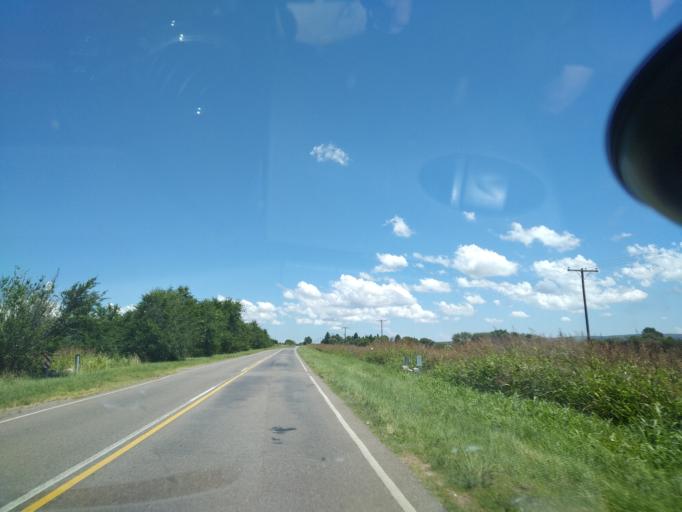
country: AR
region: Cordoba
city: Villa Cura Brochero
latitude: -31.5443
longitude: -65.1119
